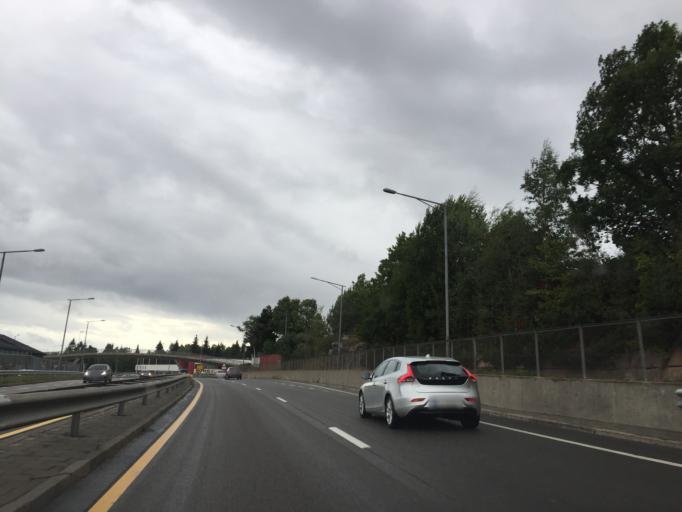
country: NO
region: Akershus
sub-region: Lorenskog
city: Kjenn
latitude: 59.9542
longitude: 10.8919
